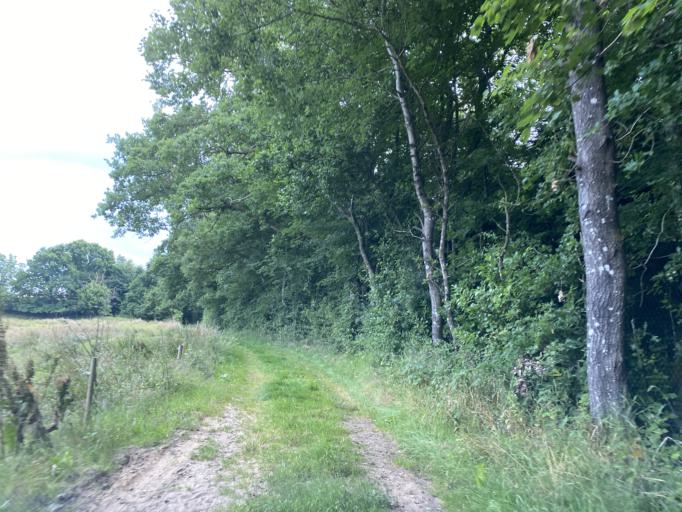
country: DK
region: Central Jutland
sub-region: Favrskov Kommune
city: Hammel
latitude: 56.2196
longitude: 9.7507
